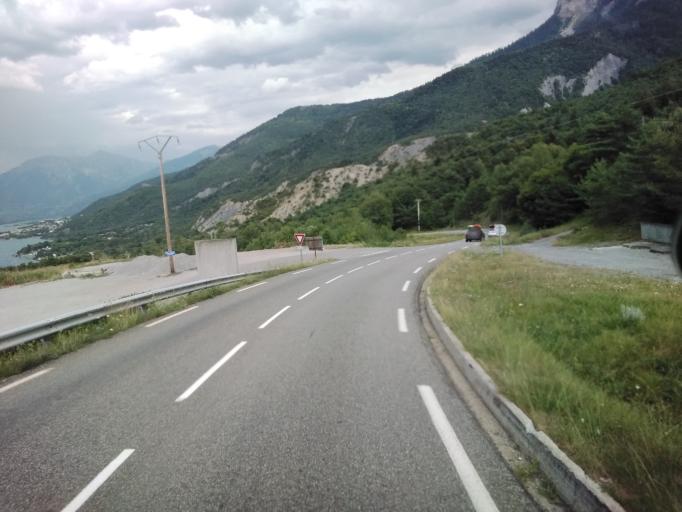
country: FR
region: Provence-Alpes-Cote d'Azur
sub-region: Departement des Hautes-Alpes
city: Chorges
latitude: 44.5138
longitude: 6.3647
